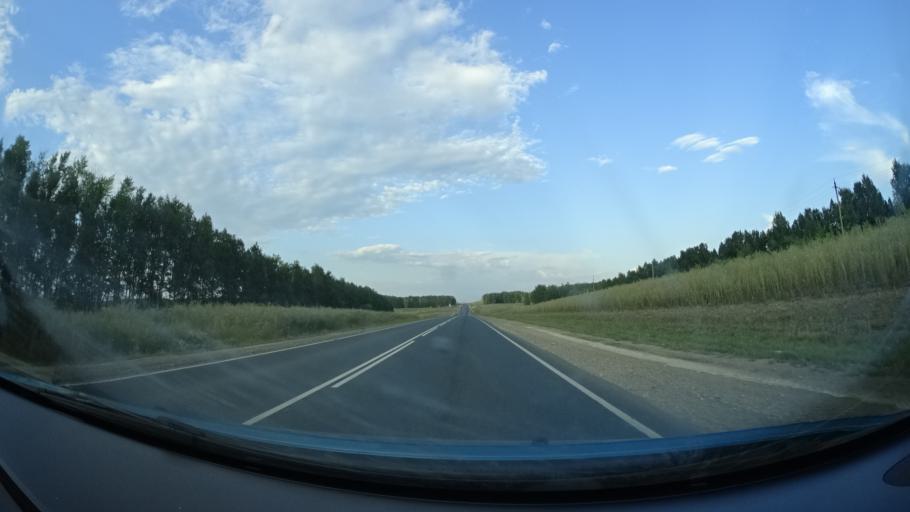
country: RU
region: Samara
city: Isakly
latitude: 54.0184
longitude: 51.7902
